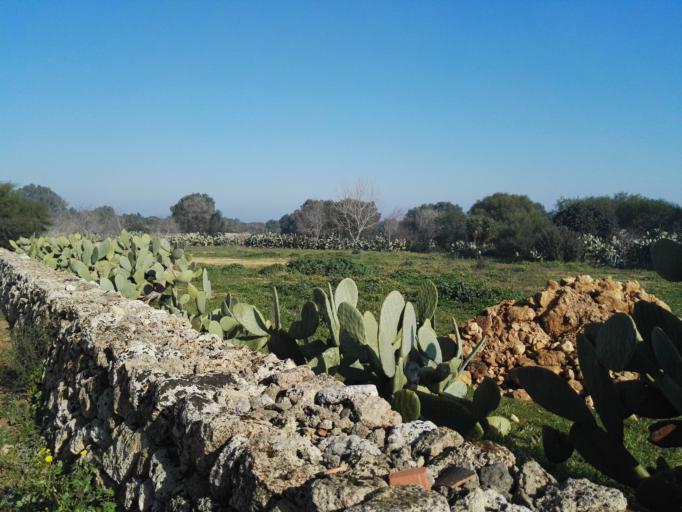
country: IT
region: Apulia
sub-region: Provincia di Lecce
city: Surbo
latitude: 40.4664
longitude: 18.1291
